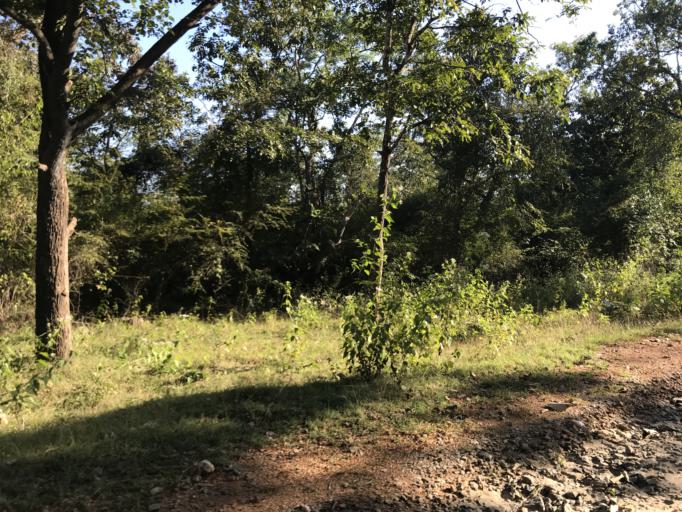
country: IN
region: Karnataka
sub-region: Mysore
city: Heggadadevankote
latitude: 11.9640
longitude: 76.2424
